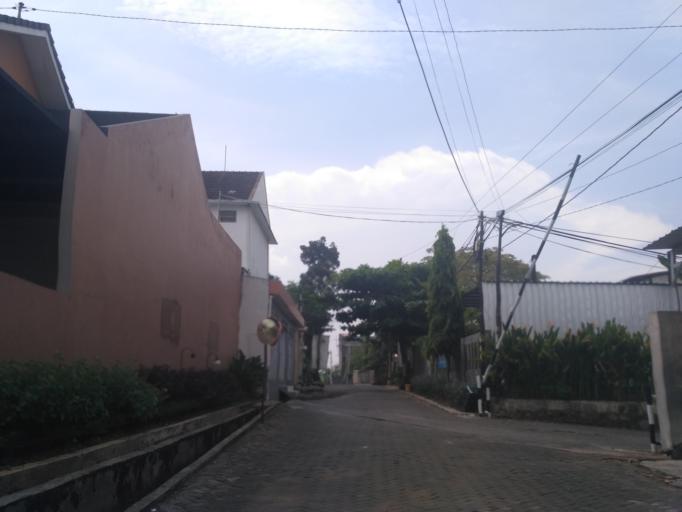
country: ID
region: Central Java
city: Ungaran
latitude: -7.0731
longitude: 110.4404
